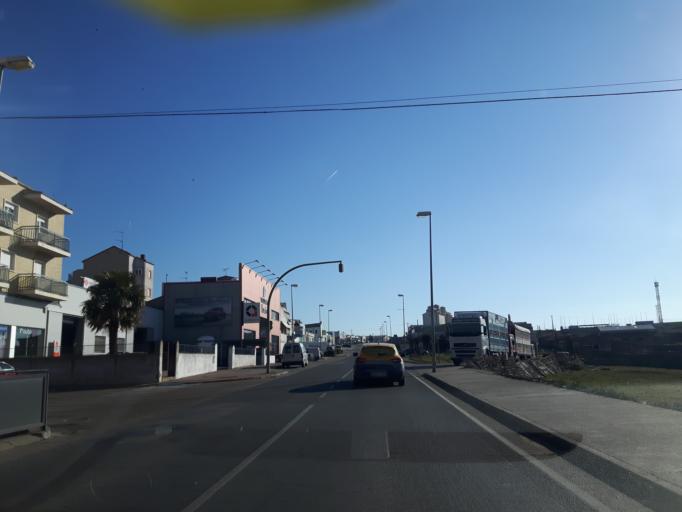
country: ES
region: Castille and Leon
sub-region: Provincia de Salamanca
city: Alba de Tormes
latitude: 40.8269
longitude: -5.5076
